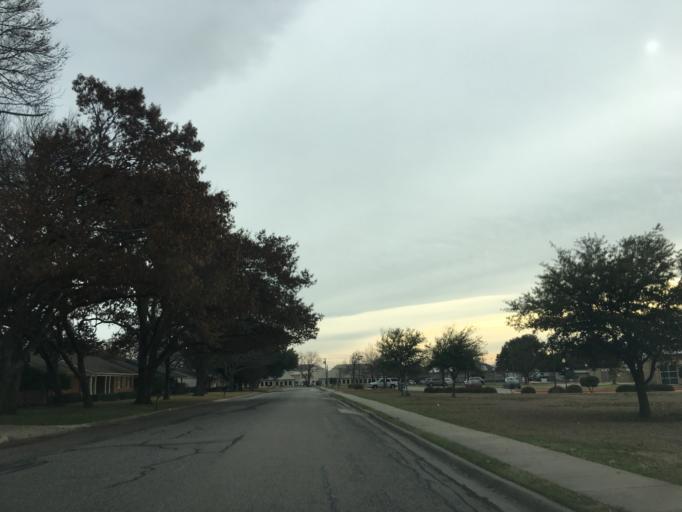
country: US
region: Texas
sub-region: Collin County
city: McKinney
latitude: 33.2015
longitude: -96.6343
